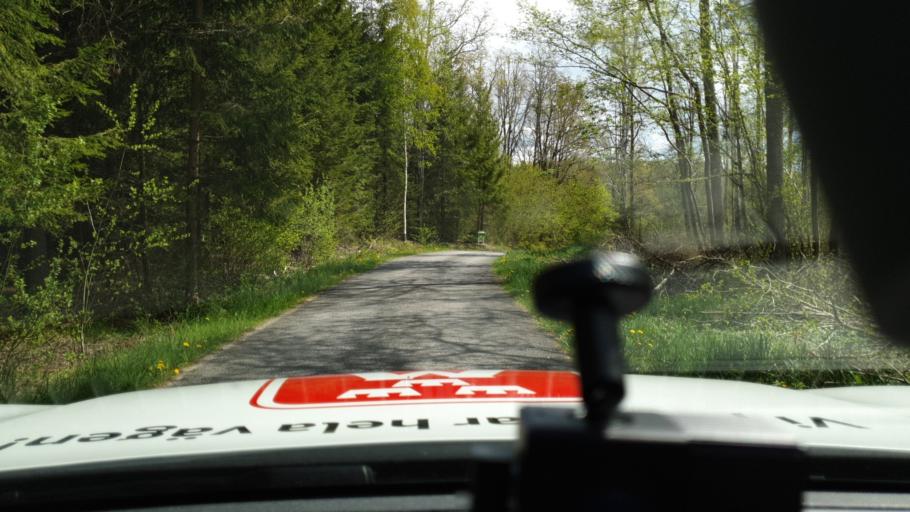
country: SE
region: Kalmar
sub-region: Vasterviks Kommun
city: Ankarsrum
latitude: 57.7820
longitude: 16.1612
